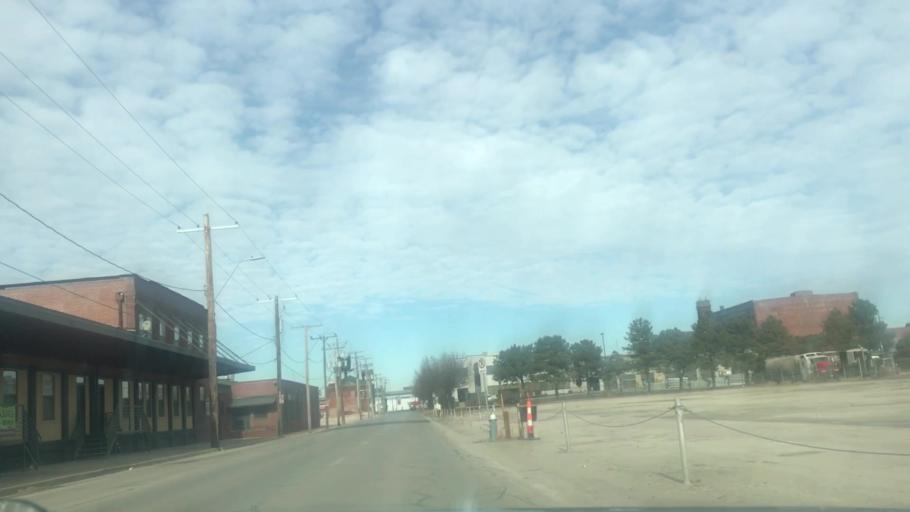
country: US
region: Missouri
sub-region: Jackson County
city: Kansas City
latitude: 39.0952
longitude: -94.6037
